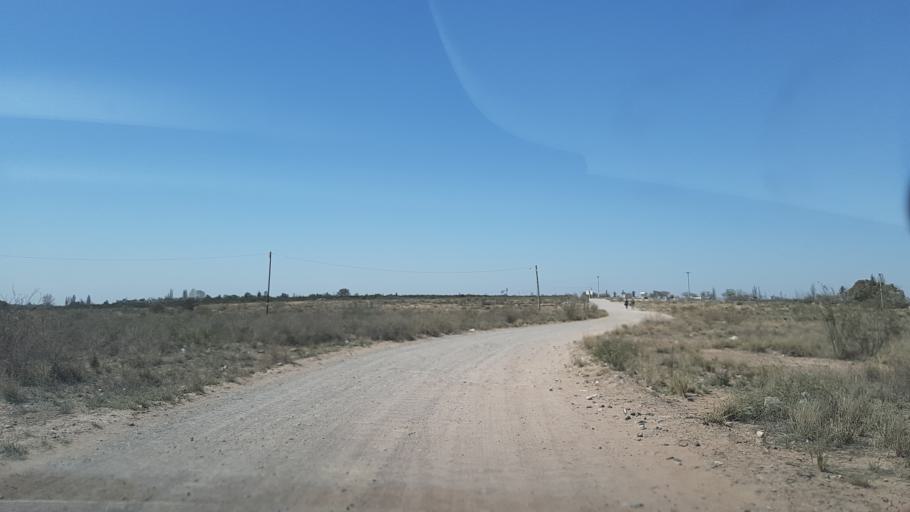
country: AR
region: Mendoza
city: Lujan de Cuyo
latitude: -33.0184
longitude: -68.9493
